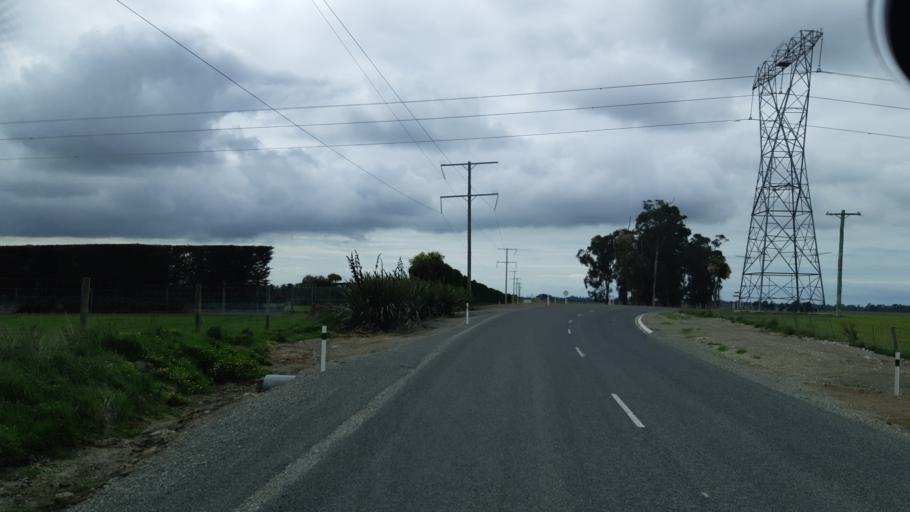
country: NZ
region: Canterbury
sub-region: Timaru District
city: Pleasant Point
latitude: -44.3527
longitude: 171.1290
